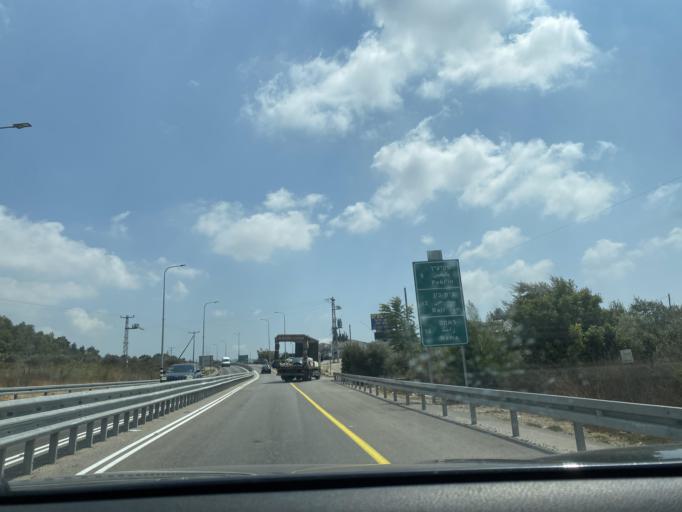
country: IL
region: Northern District
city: Kefar Weradim
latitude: 33.0034
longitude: 35.2969
